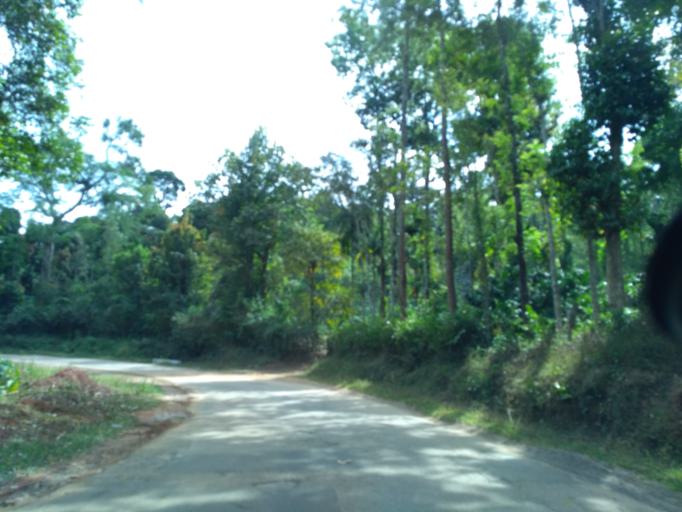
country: IN
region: Karnataka
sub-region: Kodagu
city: Madikeri
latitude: 12.3700
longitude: 75.6980
